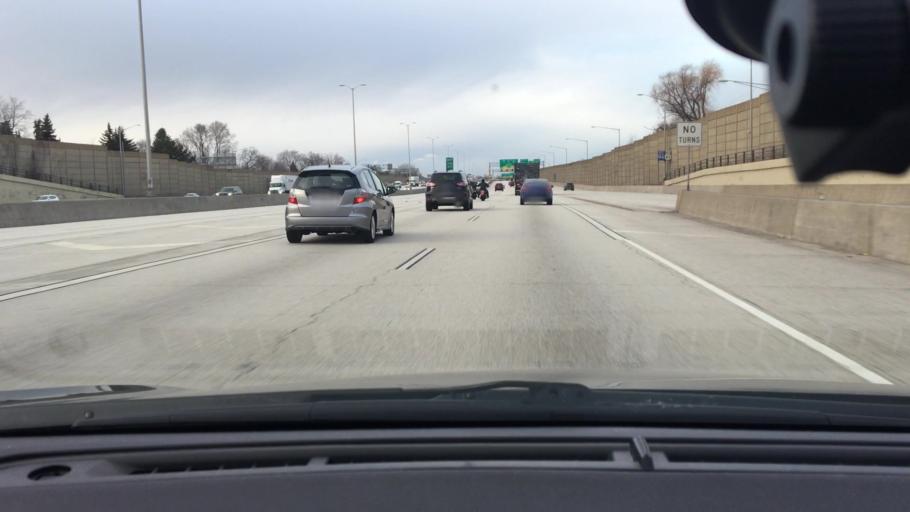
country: US
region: Wisconsin
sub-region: Milwaukee County
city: Saint Francis
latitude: 42.9463
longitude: -87.9348
